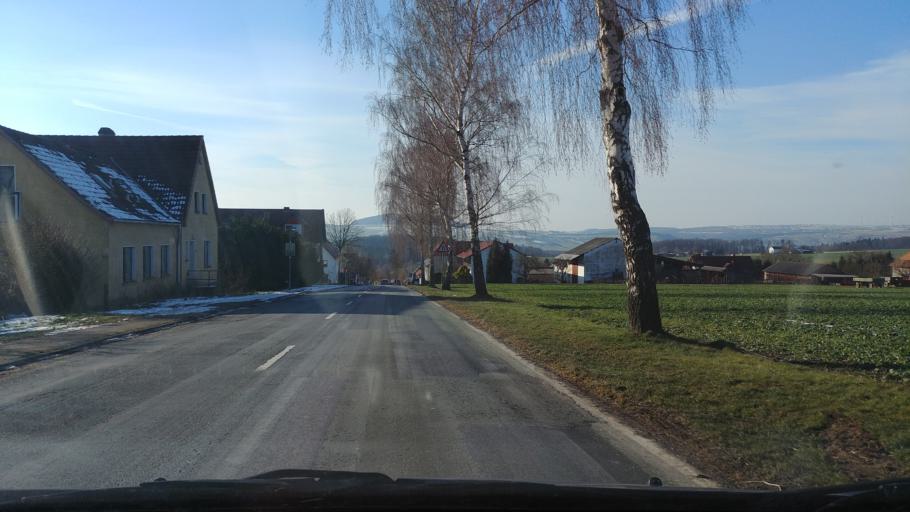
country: DE
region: Hesse
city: Trendelburg
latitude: 51.5737
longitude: 9.4649
